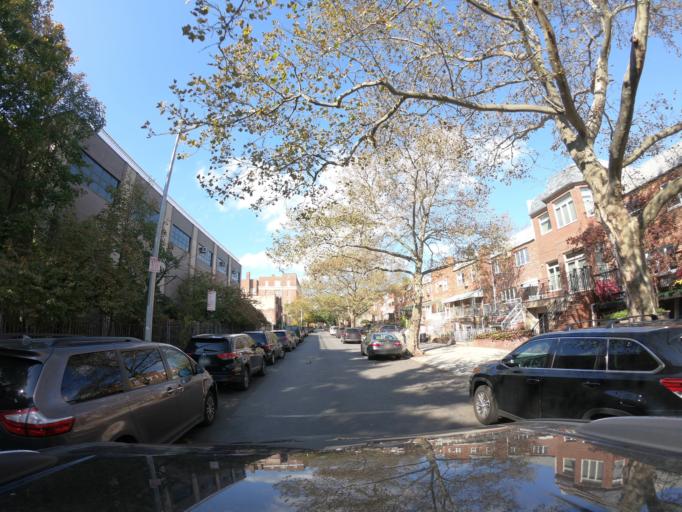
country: US
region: New York
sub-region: Kings County
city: Bensonhurst
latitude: 40.6260
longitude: -73.9877
